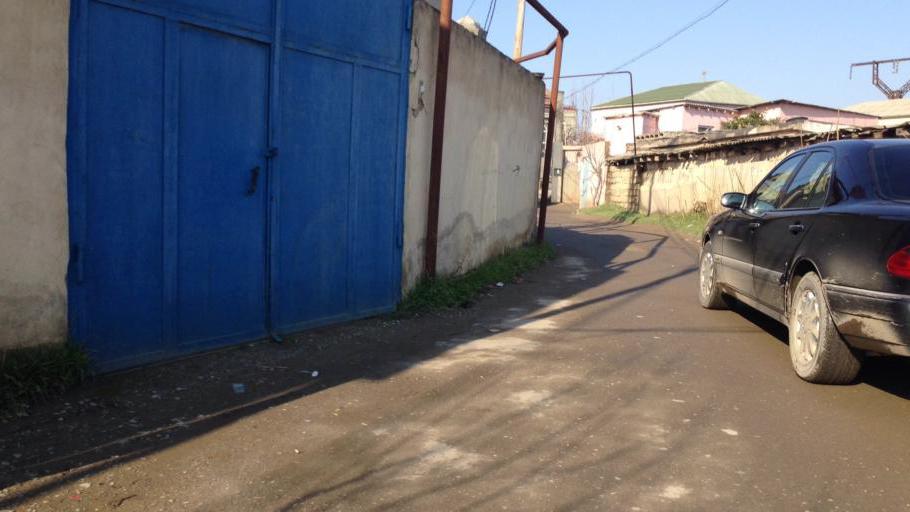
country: AZ
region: Baki
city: Binagadi
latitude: 40.4346
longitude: 49.8539
